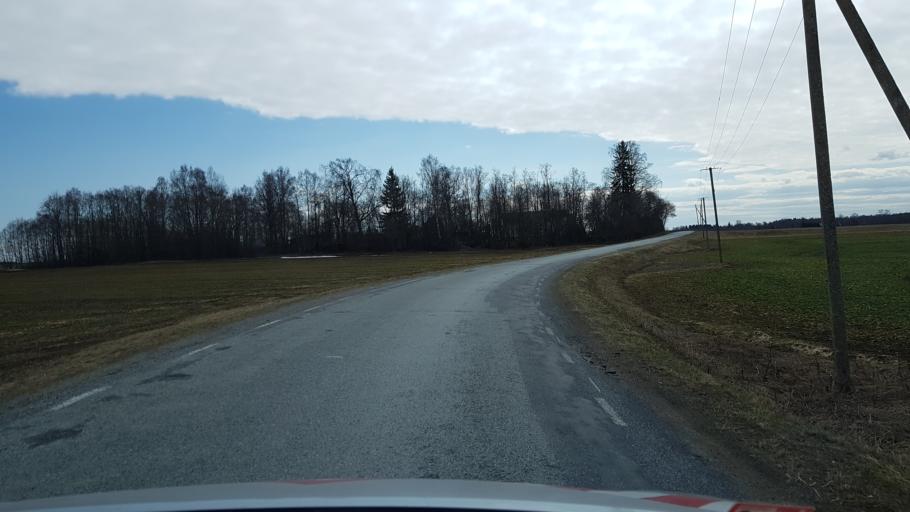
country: EE
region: Laeaene-Virumaa
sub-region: Haljala vald
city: Haljala
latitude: 59.4151
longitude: 26.2504
